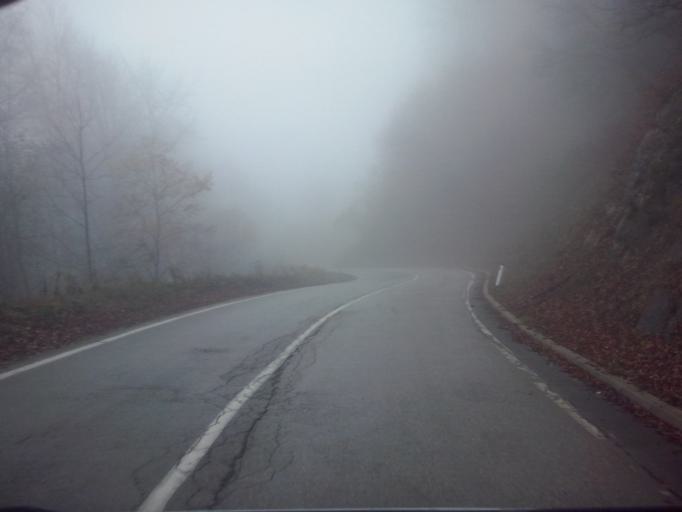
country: RS
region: Central Serbia
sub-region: Moravicki Okrug
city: Ivanjica
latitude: 43.5302
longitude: 20.3099
